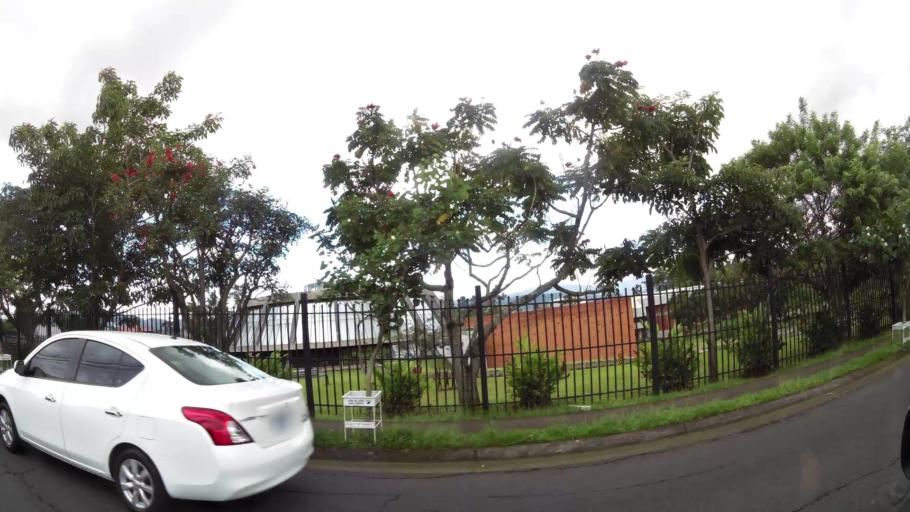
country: CR
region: San Jose
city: San Pedro
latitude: 9.9234
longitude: -84.0483
